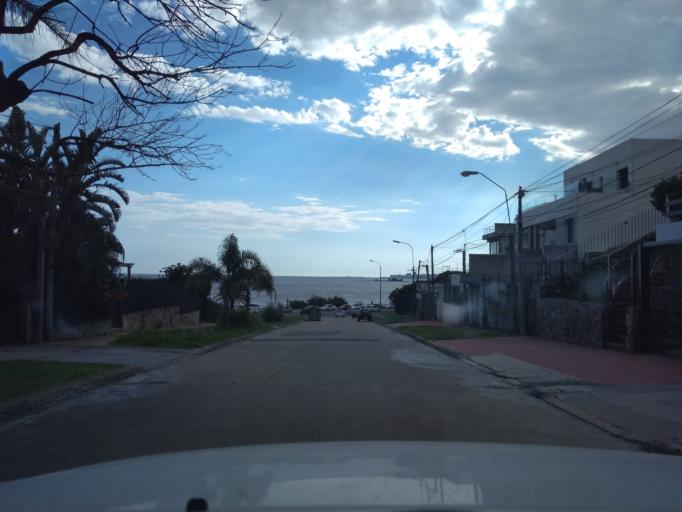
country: UY
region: Canelones
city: Paso de Carrasco
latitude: -34.8947
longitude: -56.0875
